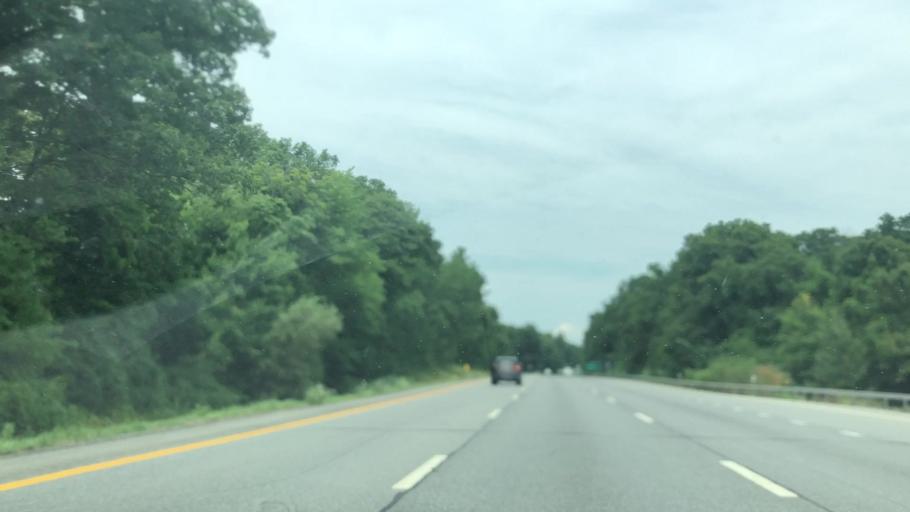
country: US
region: New York
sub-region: Albany County
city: Cohoes
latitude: 42.8230
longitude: -73.7678
